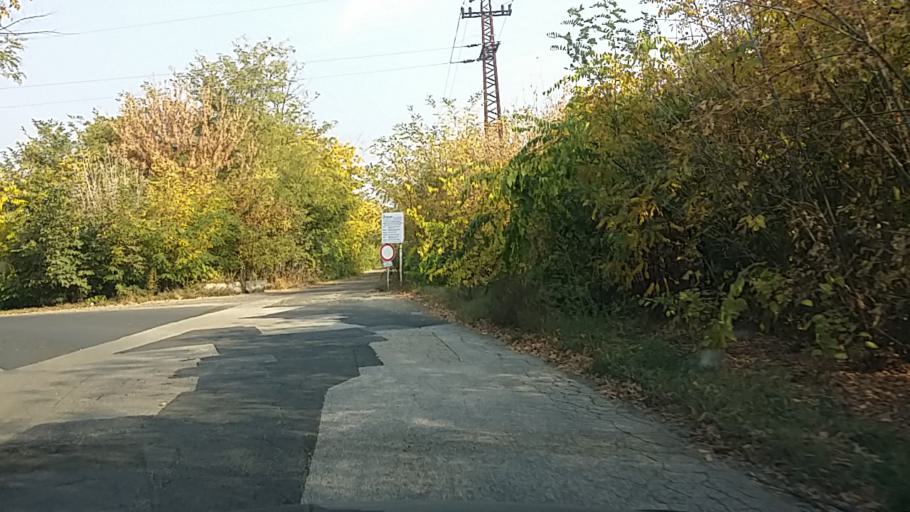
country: HU
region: Pest
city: Fot
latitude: 47.6132
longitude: 19.1625
